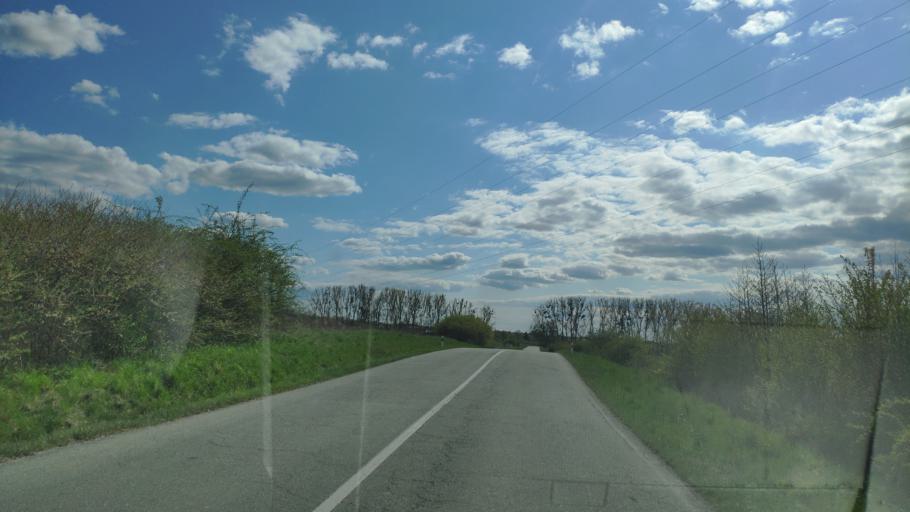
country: SK
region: Kosicky
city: Kosice
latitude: 48.6751
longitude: 21.4194
